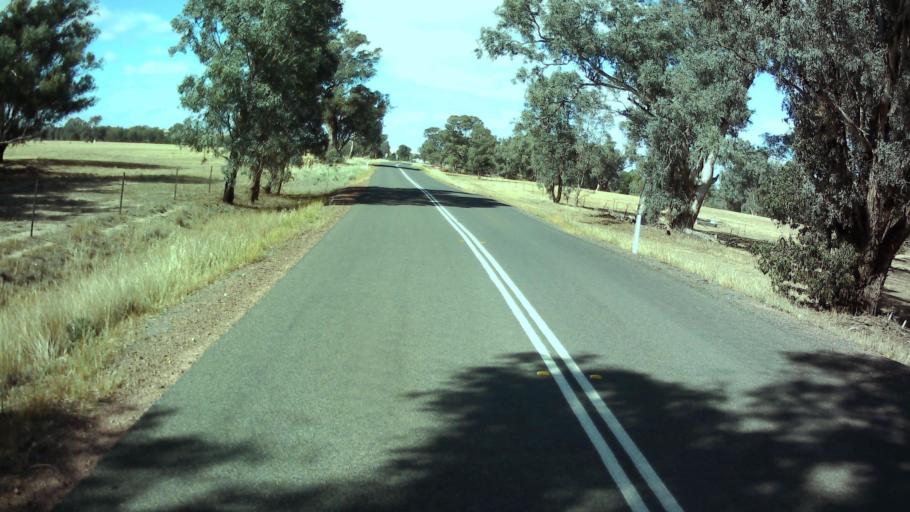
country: AU
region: New South Wales
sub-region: Weddin
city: Grenfell
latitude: -33.9897
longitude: 148.4091
